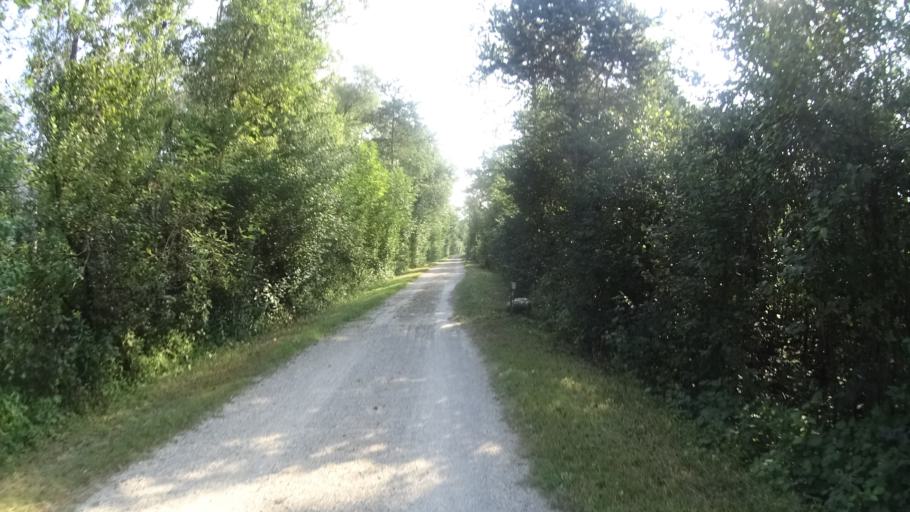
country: AT
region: Carinthia
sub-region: Politischer Bezirk Klagenfurt Land
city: Feistritz im Rosental
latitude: 46.5407
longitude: 14.1989
